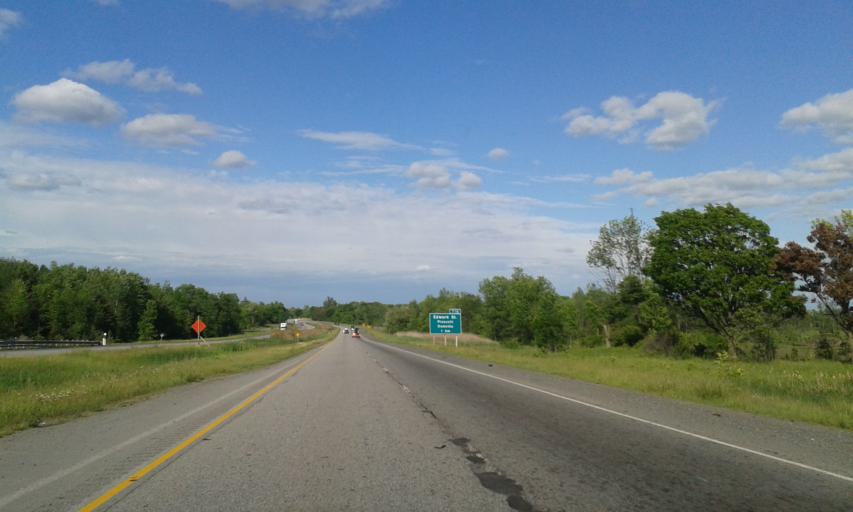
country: CA
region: Ontario
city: Prescott
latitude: 44.7170
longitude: -75.5409
